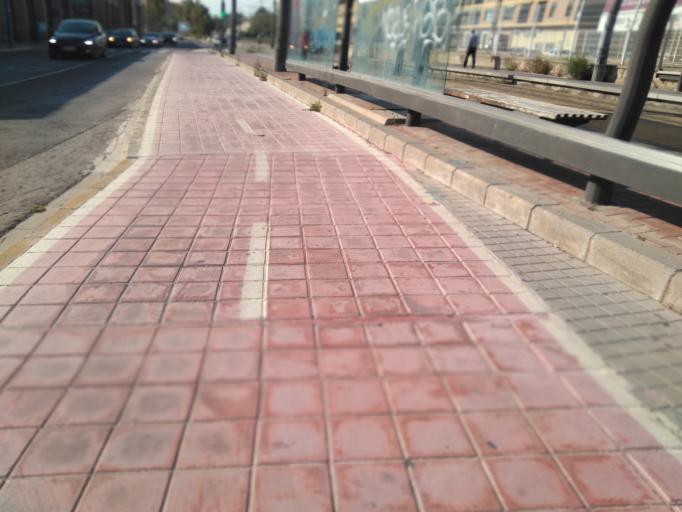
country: ES
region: Valencia
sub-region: Provincia de Valencia
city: Burjassot
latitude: 39.5005
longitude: -0.4035
